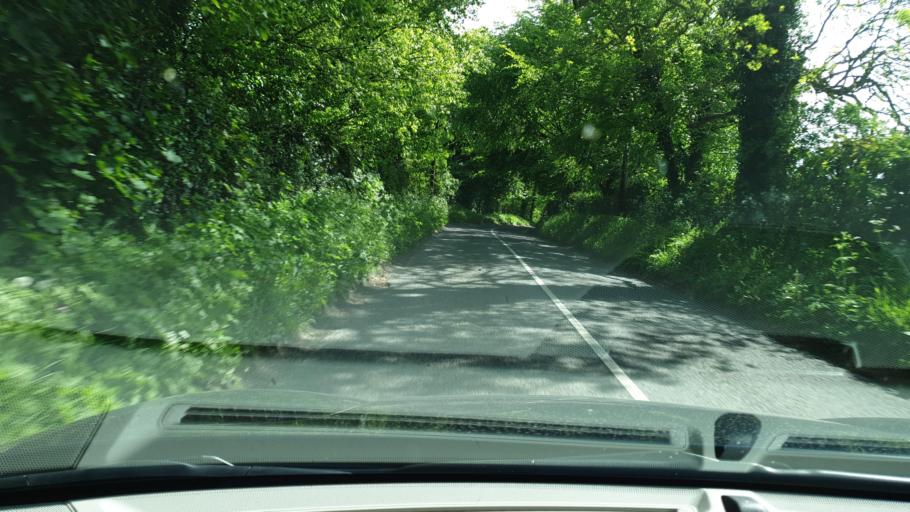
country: IE
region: Leinster
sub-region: Kildare
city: Maynooth
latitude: 53.3960
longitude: -6.5810
